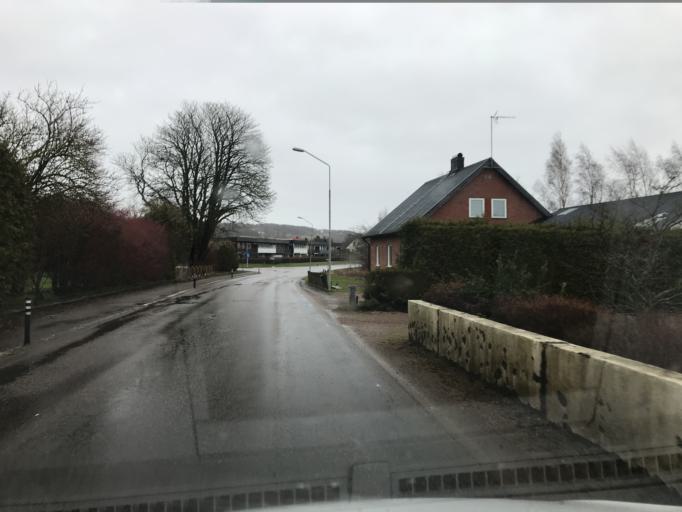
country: SE
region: Skane
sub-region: Bastads Kommun
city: Forslov
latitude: 56.3541
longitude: 12.8235
